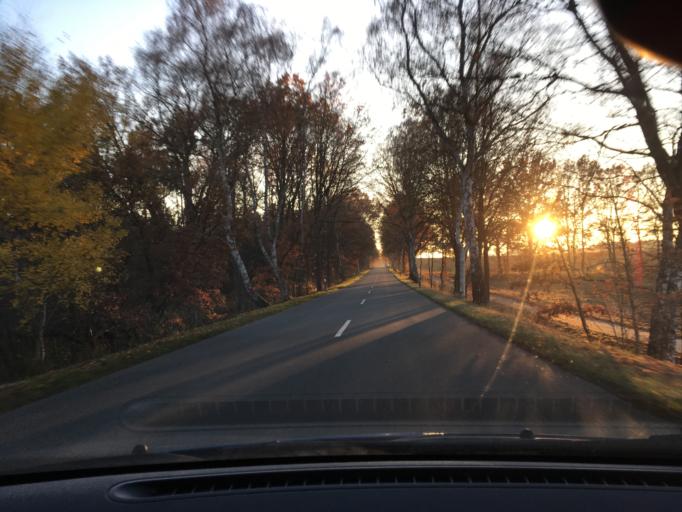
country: DE
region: Lower Saxony
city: Bienenbuttel
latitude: 53.1189
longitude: 10.4664
